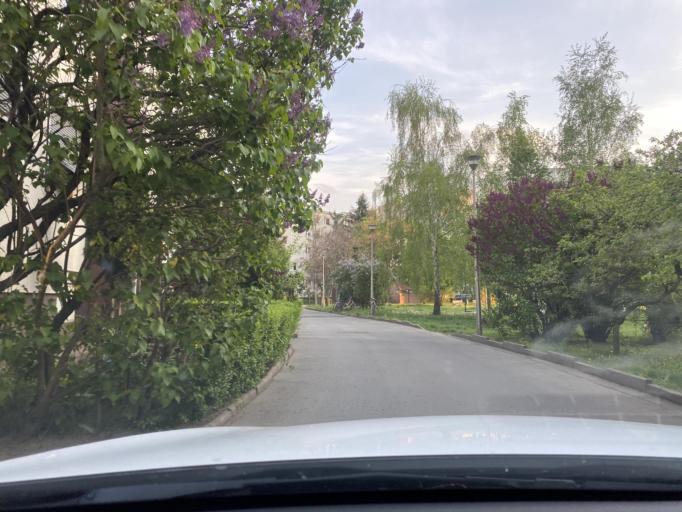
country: PL
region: Lower Silesian Voivodeship
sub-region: Powiat wroclawski
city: Wroclaw
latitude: 51.1403
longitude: 17.0250
